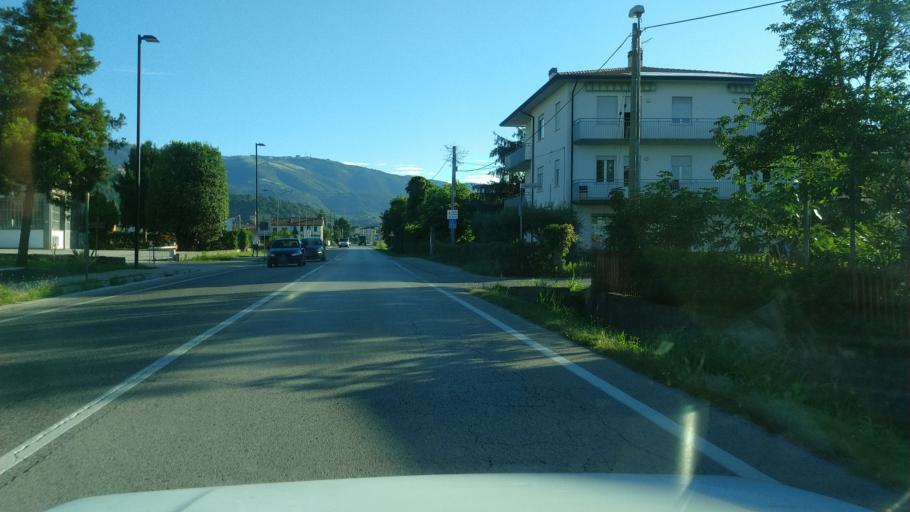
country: IT
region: Veneto
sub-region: Provincia di Vicenza
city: Marostica
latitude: 45.7349
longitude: 11.6541
